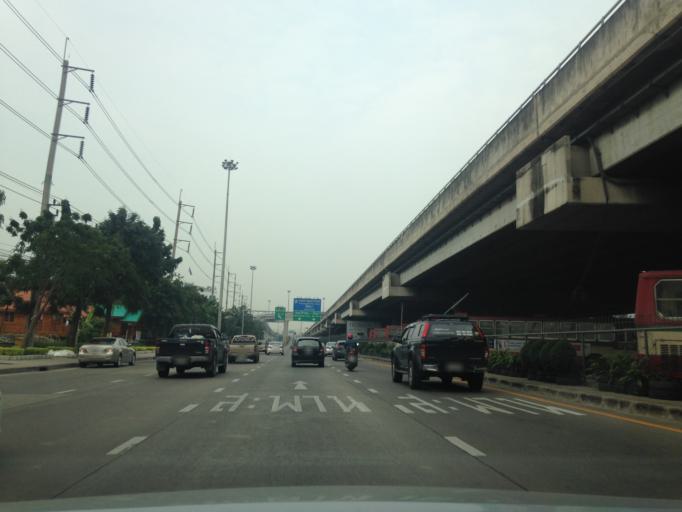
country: TH
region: Bangkok
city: Bang Khen
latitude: 13.8455
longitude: 100.6371
